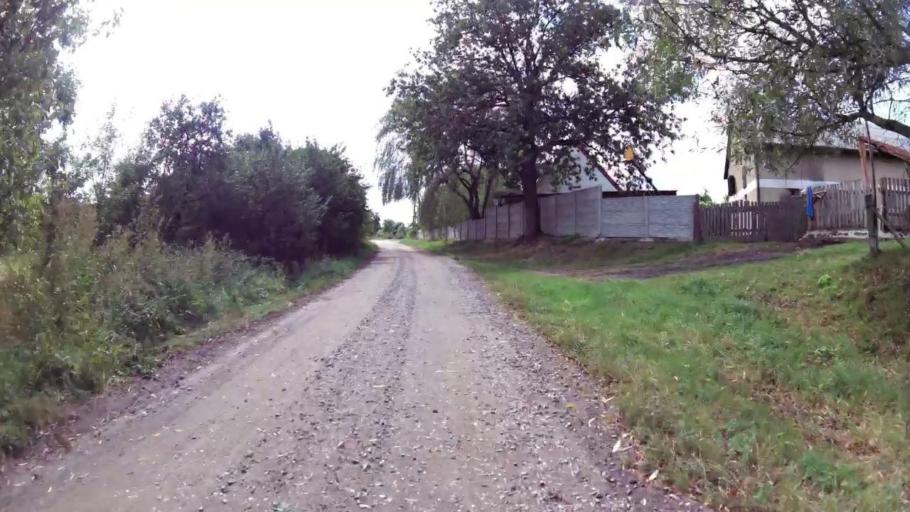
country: PL
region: West Pomeranian Voivodeship
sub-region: Powiat mysliborski
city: Debno
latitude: 52.7908
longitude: 14.6948
